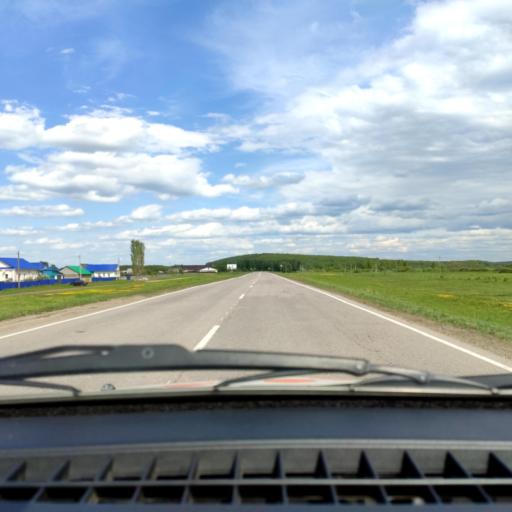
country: RU
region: Bashkortostan
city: Krasnaya Gorka
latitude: 55.0621
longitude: 56.5777
